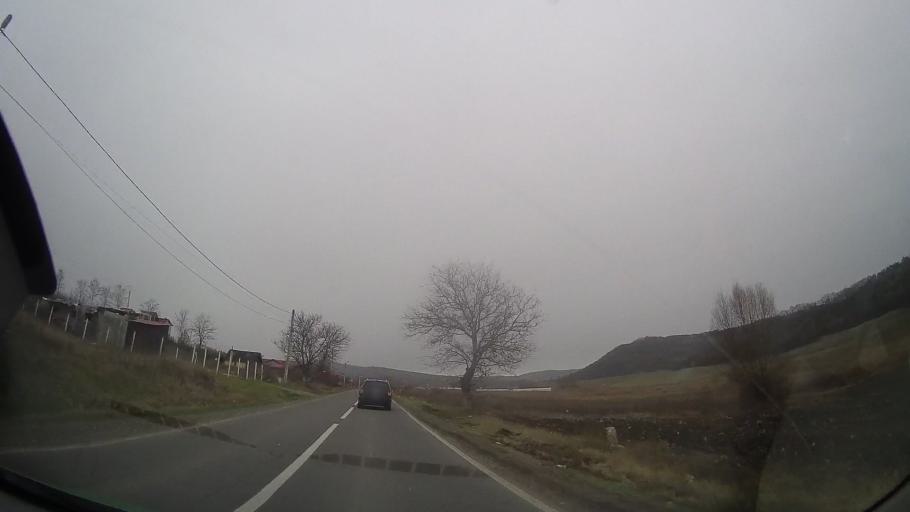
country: RO
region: Mures
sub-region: Comuna Ceausu de Campie
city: Ceausu de Campie
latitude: 46.6261
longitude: 24.5216
